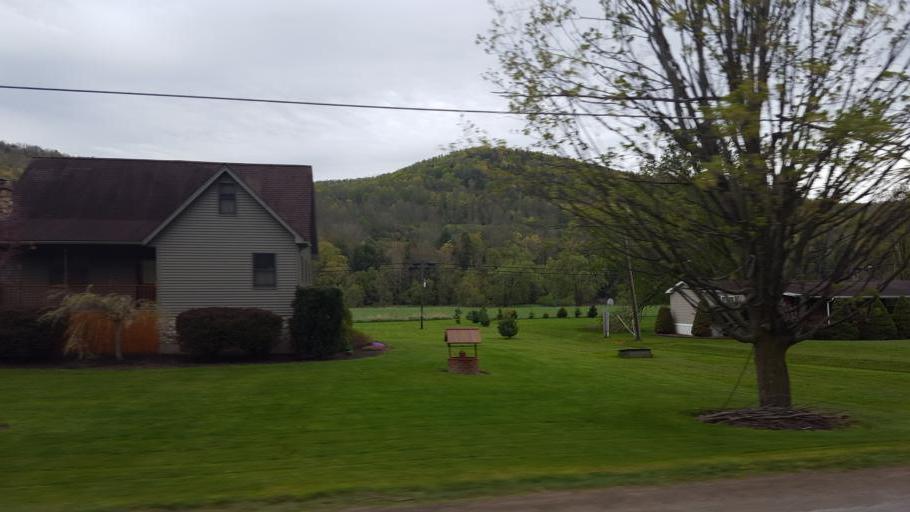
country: US
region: Pennsylvania
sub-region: Tioga County
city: Westfield
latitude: 41.9293
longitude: -77.5084
